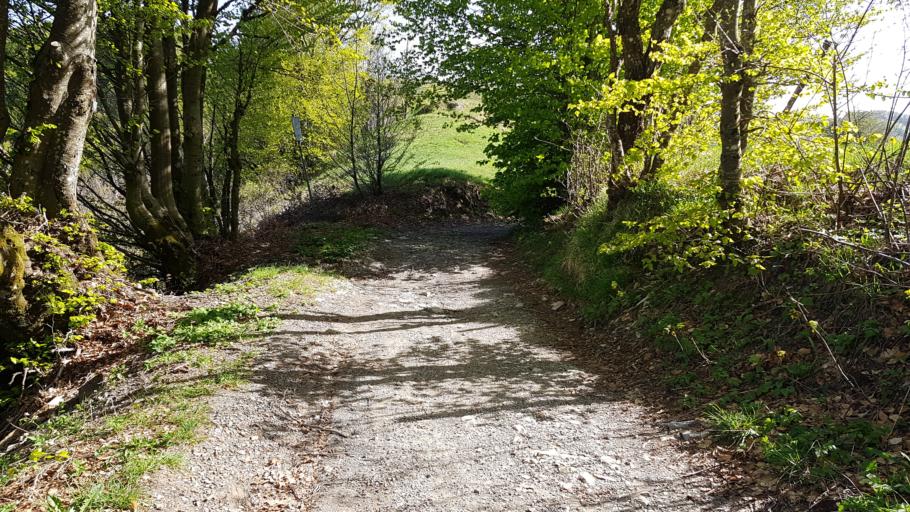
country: IT
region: Liguria
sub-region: Provincia di Genova
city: Fascia
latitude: 44.6025
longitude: 9.2051
